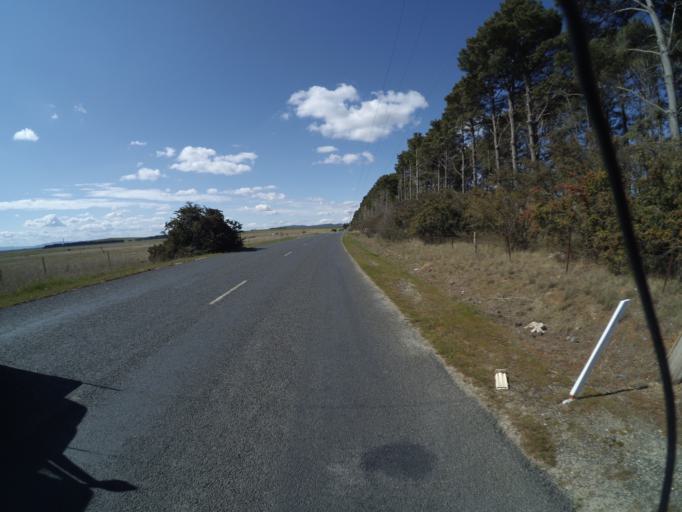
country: AU
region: New South Wales
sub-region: Palerang
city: Bungendore
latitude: -35.2277
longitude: 149.4513
